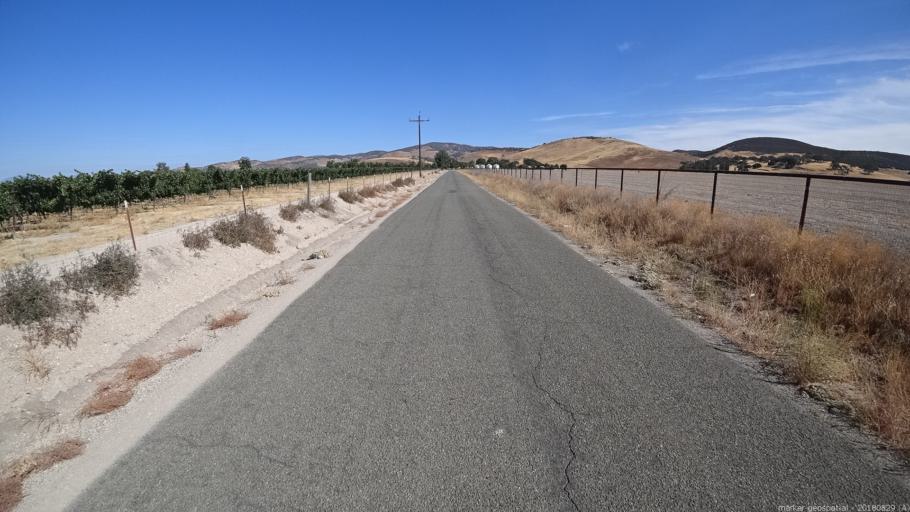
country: US
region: California
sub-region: Monterey County
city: King City
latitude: 35.9629
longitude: -121.0818
